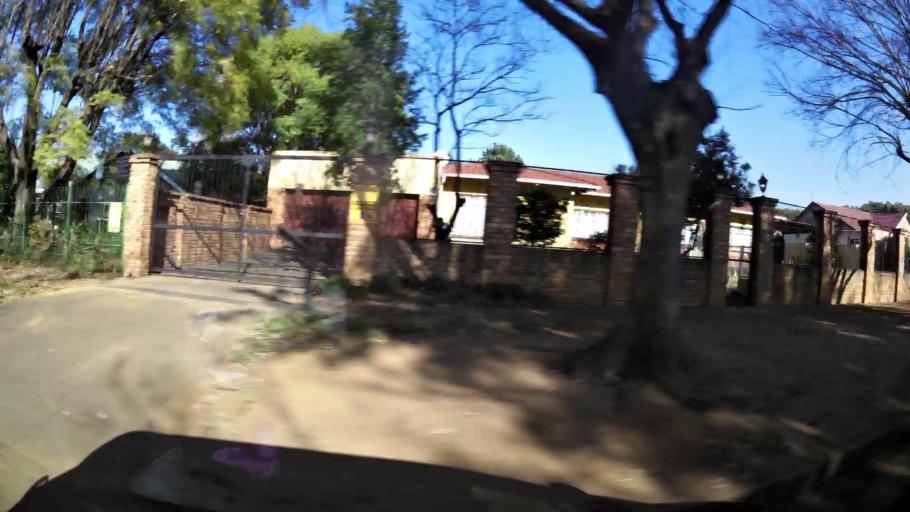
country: ZA
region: Gauteng
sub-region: Ekurhuleni Metropolitan Municipality
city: Benoni
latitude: -26.1539
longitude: 28.3218
